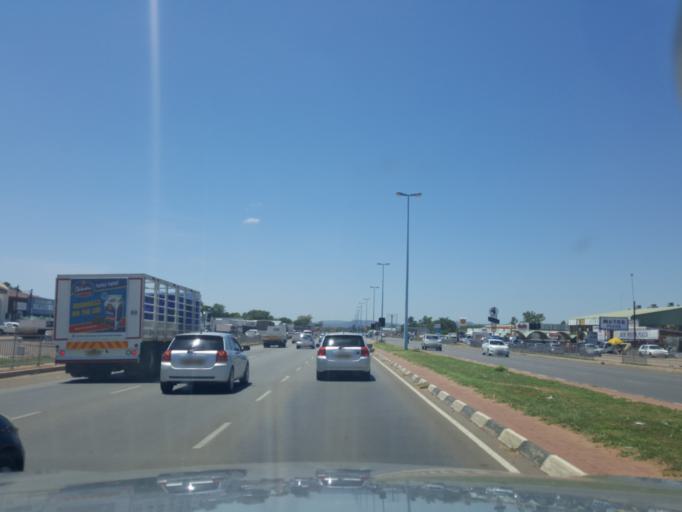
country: BW
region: Kweneng
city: Mogoditshane
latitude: -24.6247
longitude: 25.8691
